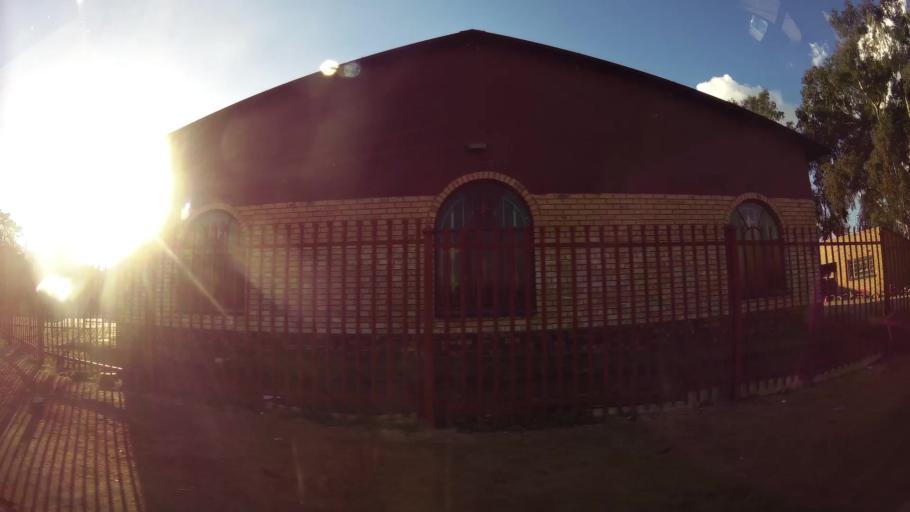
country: ZA
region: Mpumalanga
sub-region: Nkangala District Municipality
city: Witbank
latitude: -25.8739
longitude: 29.1810
